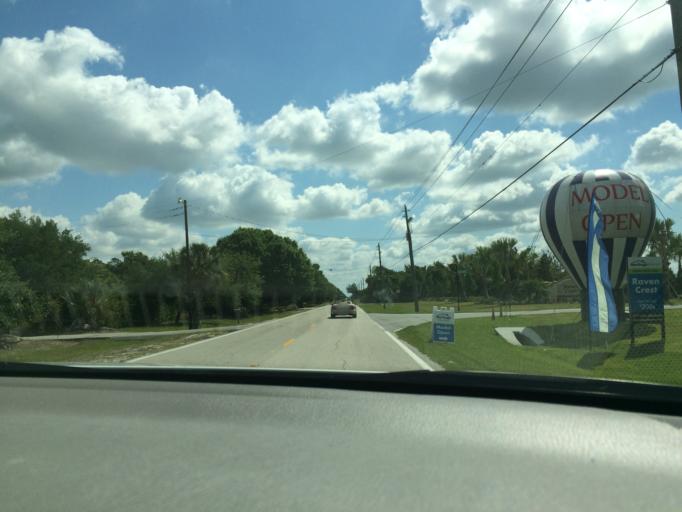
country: US
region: Florida
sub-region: Manatee County
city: Ellenton
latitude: 27.5138
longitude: -82.4251
